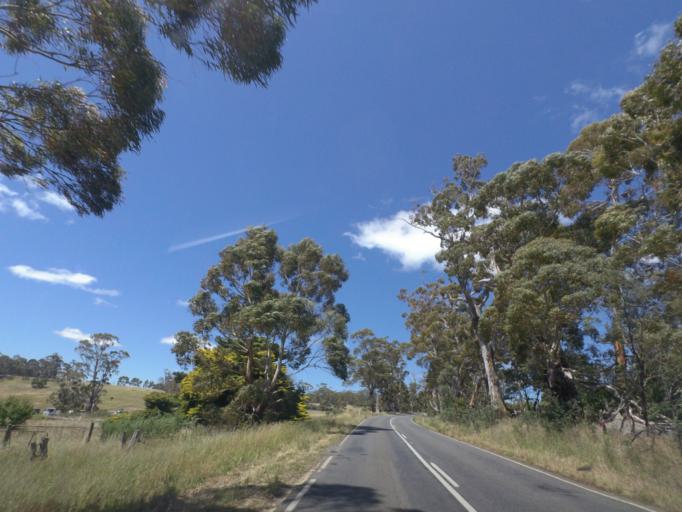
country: AU
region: Victoria
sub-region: Mount Alexander
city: Castlemaine
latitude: -37.2917
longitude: 144.2495
